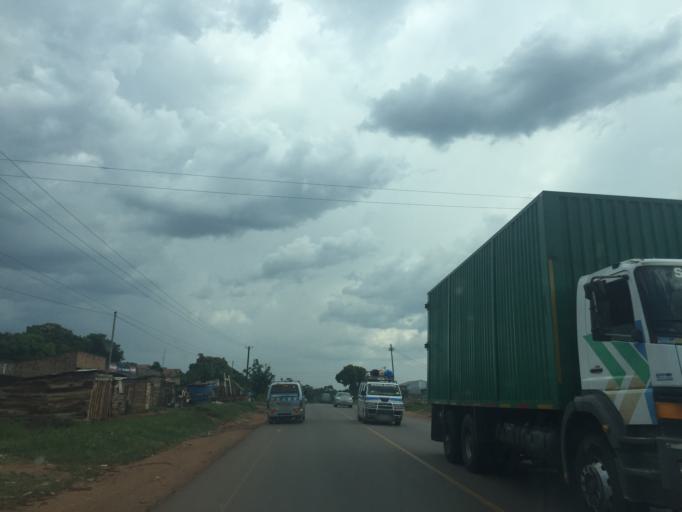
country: UG
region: Central Region
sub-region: Luwero District
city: Wobulenzi
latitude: 0.6792
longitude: 32.5257
